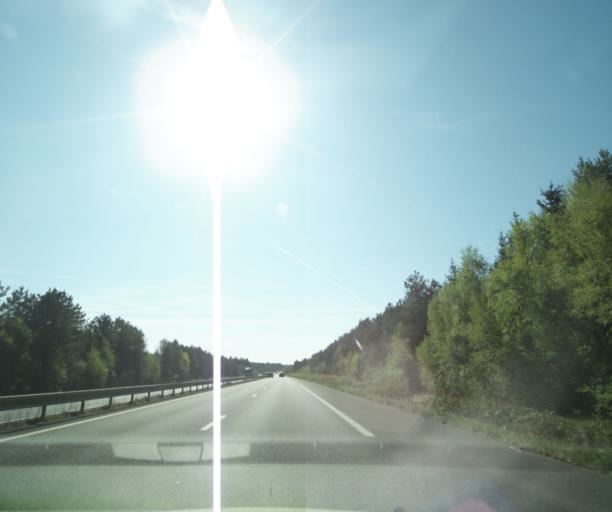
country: FR
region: Centre
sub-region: Departement du Loir-et-Cher
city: Lamotte-Beuvron
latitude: 47.6017
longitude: 1.9752
